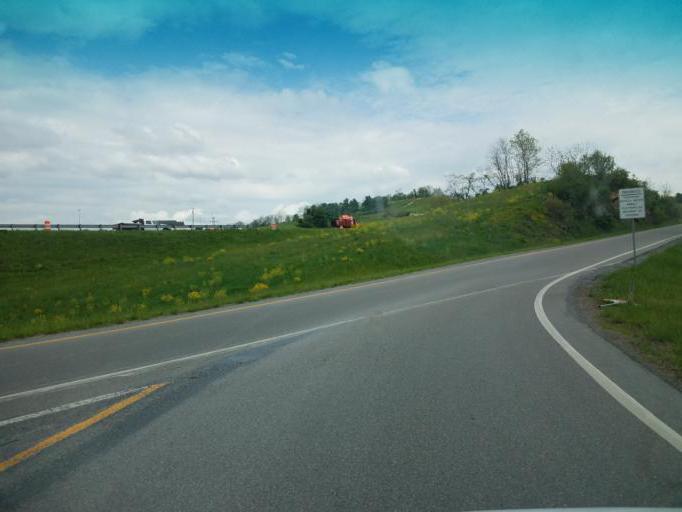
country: US
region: Virginia
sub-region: Smyth County
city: Marion
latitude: 36.8265
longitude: -81.5059
